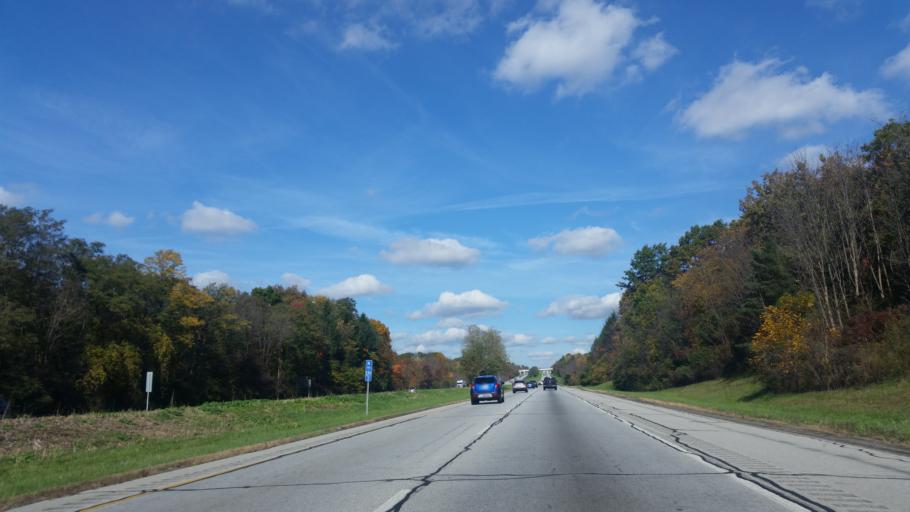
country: US
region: Ohio
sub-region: Summit County
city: Montrose-Ghent
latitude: 41.1638
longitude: -81.6259
